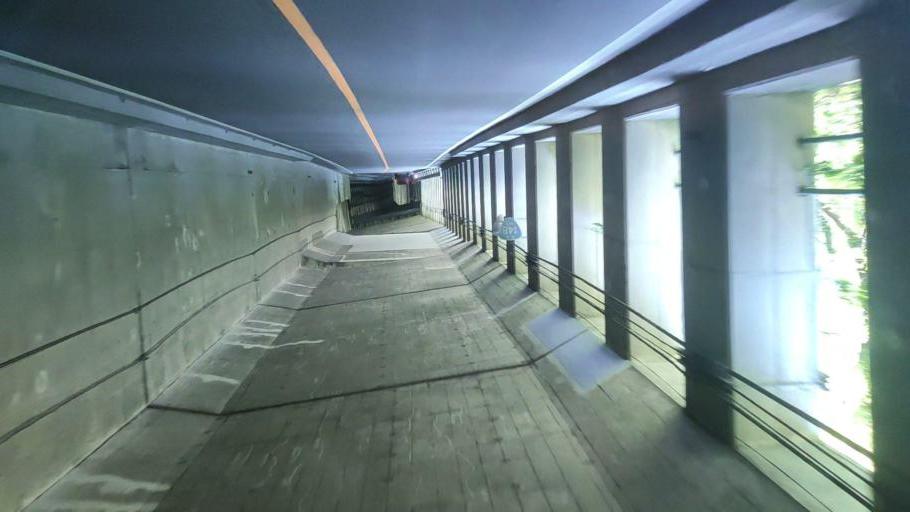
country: JP
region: Niigata
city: Itoigawa
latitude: 36.9091
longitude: 137.8625
